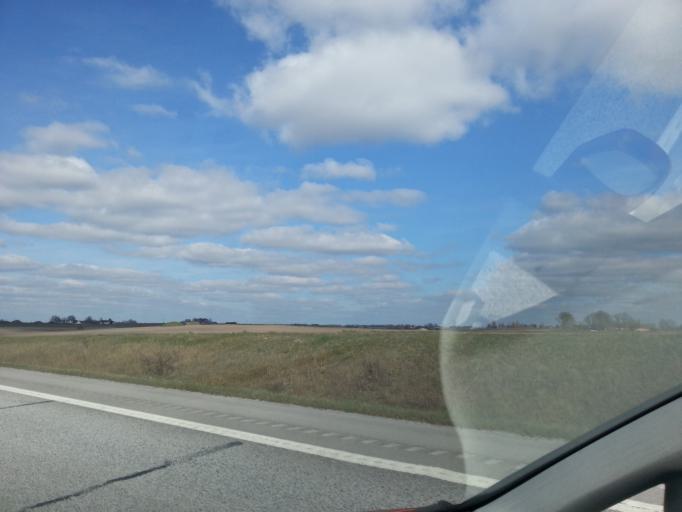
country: SE
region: Skane
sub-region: Malmo
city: Tygelsjo
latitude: 55.5015
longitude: 13.0191
